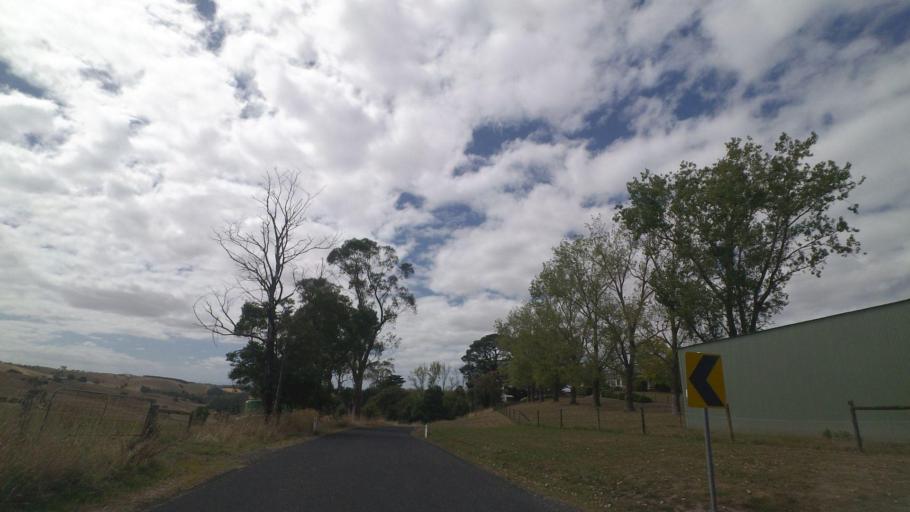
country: AU
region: Victoria
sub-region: Bass Coast
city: North Wonthaggi
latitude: -38.4023
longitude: 145.7667
